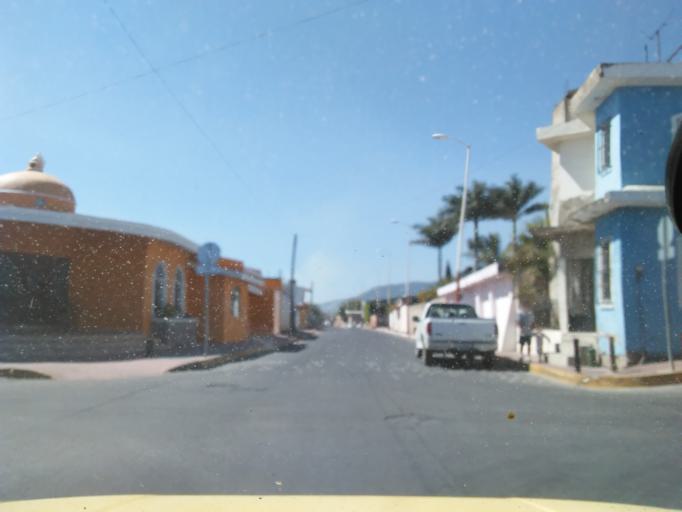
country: MX
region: Nayarit
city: Xalisco
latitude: 21.4437
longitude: -104.8980
